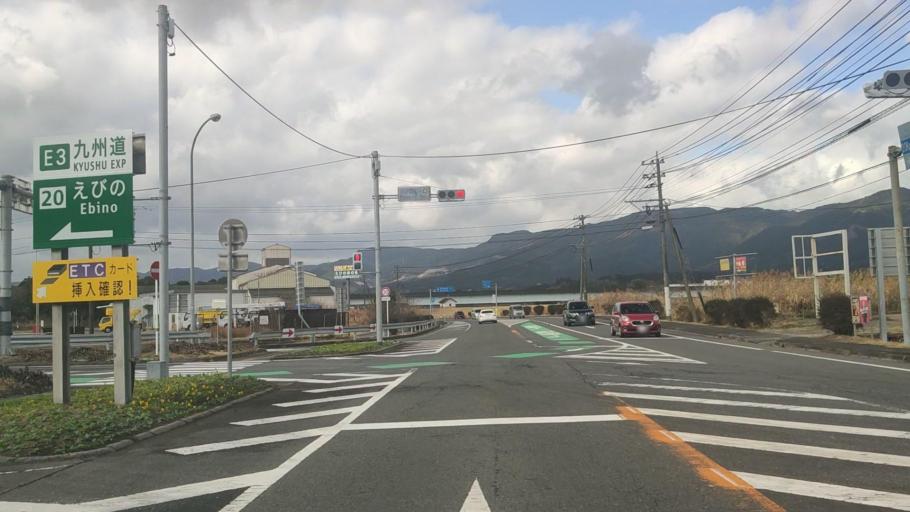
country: JP
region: Kumamoto
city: Hitoyoshi
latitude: 32.0519
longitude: 130.8045
